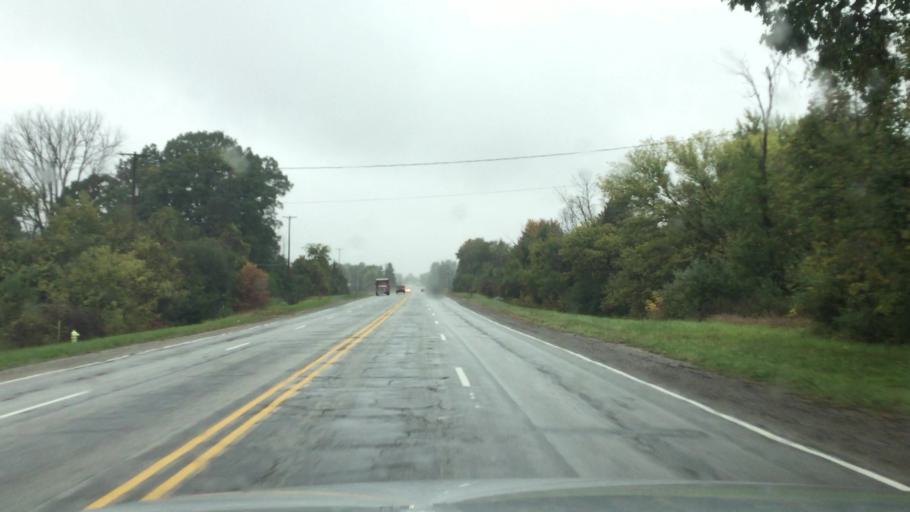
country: US
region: Michigan
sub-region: Saginaw County
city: Bridgeport
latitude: 43.3231
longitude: -83.8244
